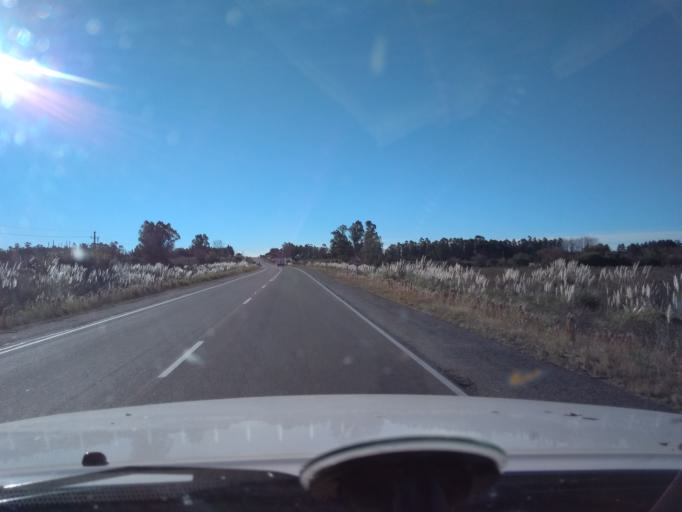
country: UY
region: Canelones
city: Sauce
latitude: -34.5966
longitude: -56.0511
